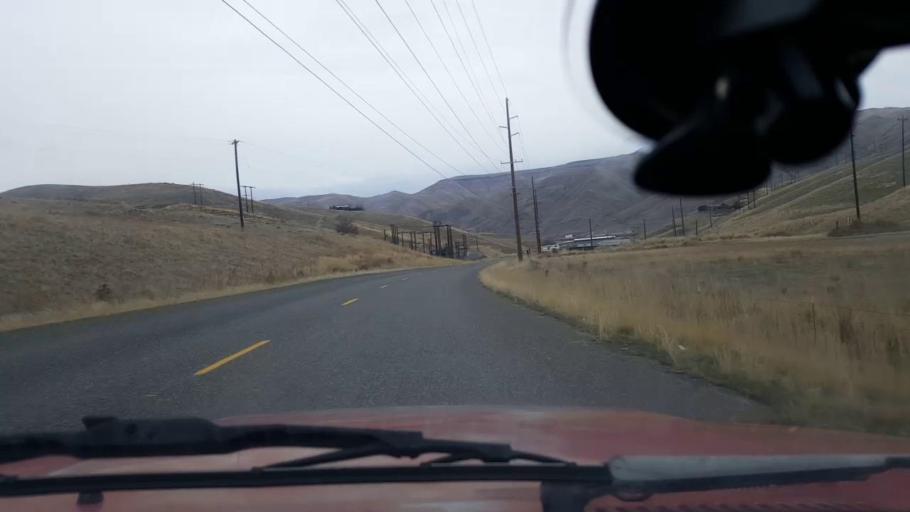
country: US
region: Washington
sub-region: Asotin County
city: Clarkston Heights-Vineland
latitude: 46.4097
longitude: -117.1104
